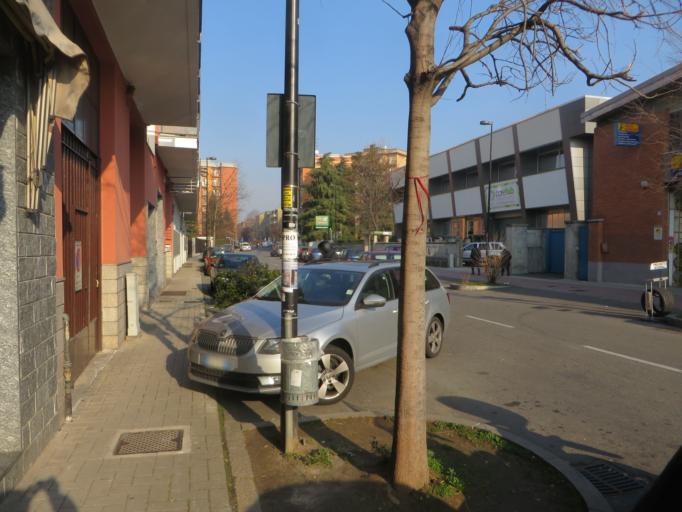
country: IT
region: Lombardy
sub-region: Citta metropolitana di Milano
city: Cormano
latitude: 45.5450
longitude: 9.1607
